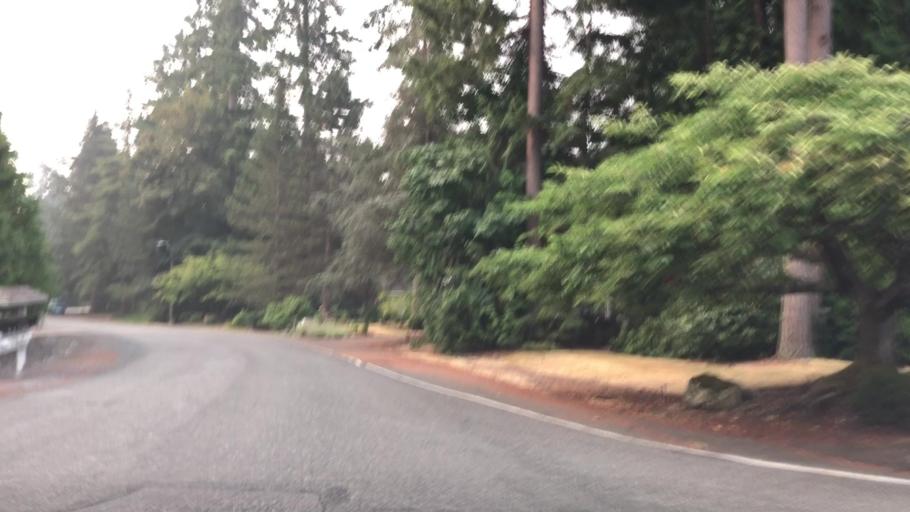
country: US
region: Washington
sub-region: King County
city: Cottage Lake
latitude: 47.7250
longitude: -122.1010
